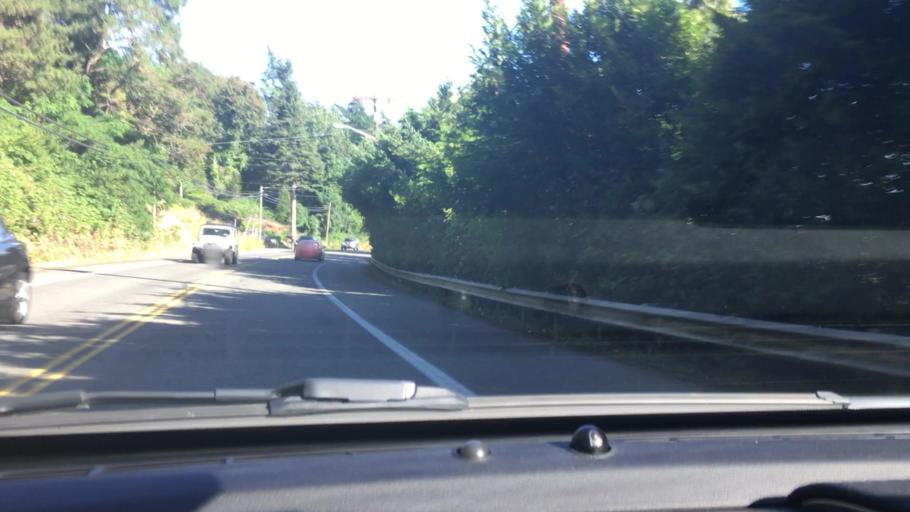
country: US
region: Washington
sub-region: King County
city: Sammamish
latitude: 47.6455
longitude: -122.0844
